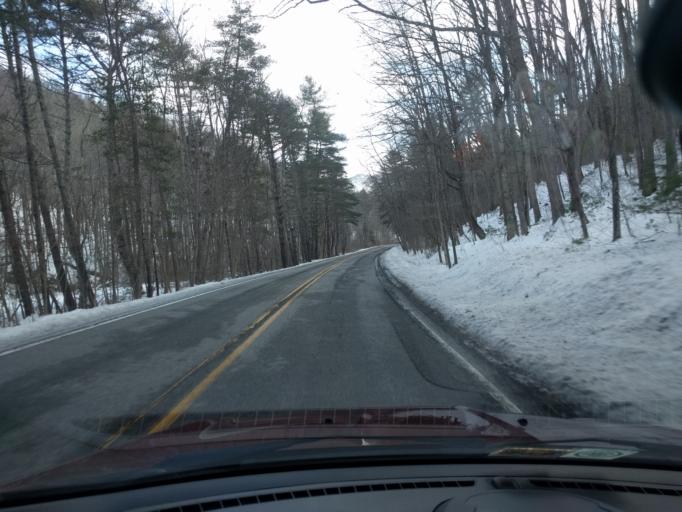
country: US
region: Virginia
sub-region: Bath County
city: Warm Springs
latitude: 38.1237
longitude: -79.9340
